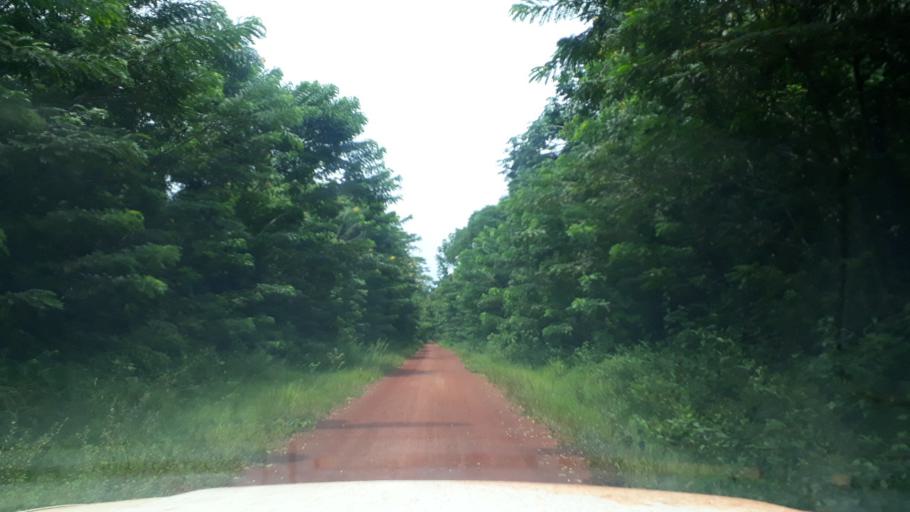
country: CD
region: Eastern Province
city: Aketi
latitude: 2.9316
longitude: 24.0914
